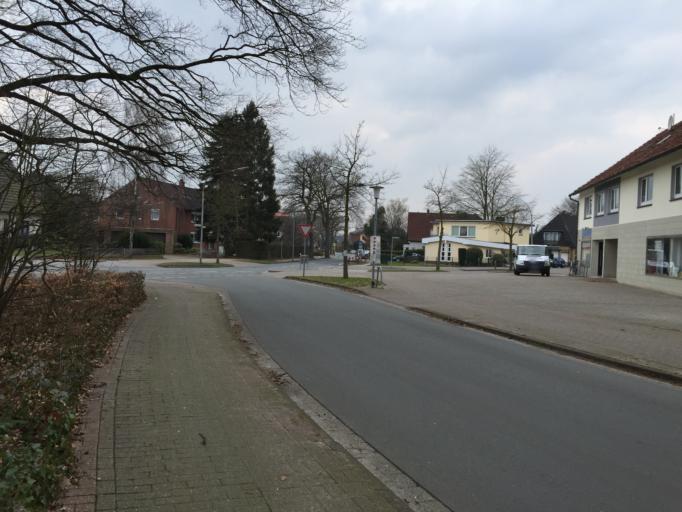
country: DE
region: Lower Saxony
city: Oldenburg
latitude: 53.1678
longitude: 8.2437
